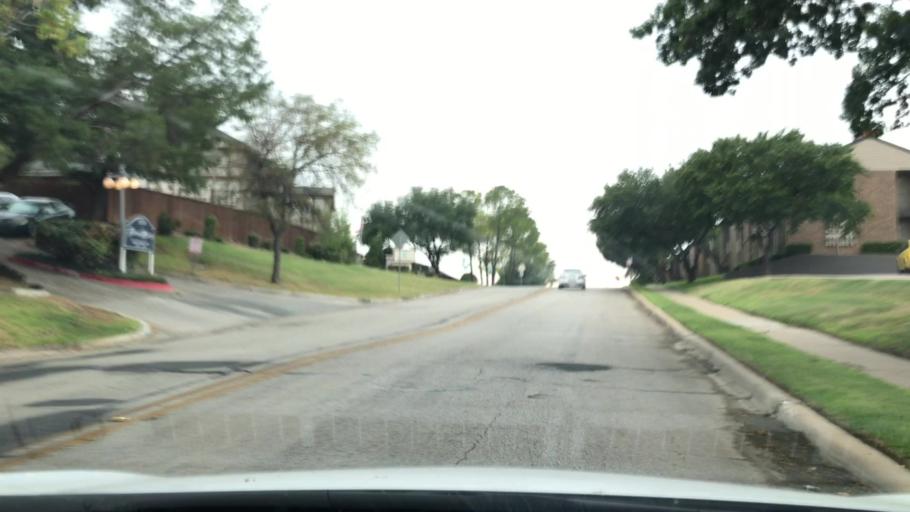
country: US
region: Texas
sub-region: Dallas County
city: Irving
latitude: 32.8606
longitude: -96.9935
